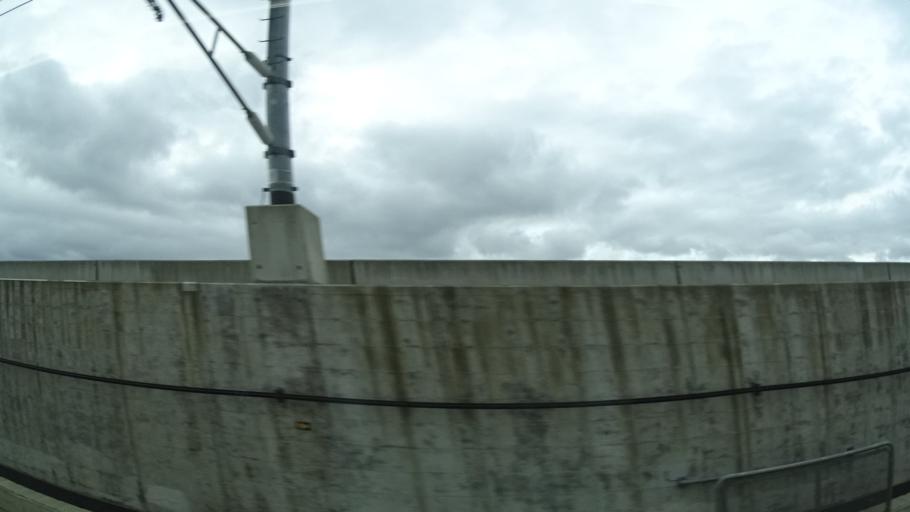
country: JP
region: Nagano
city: Suzaka
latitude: 36.7196
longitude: 138.3001
